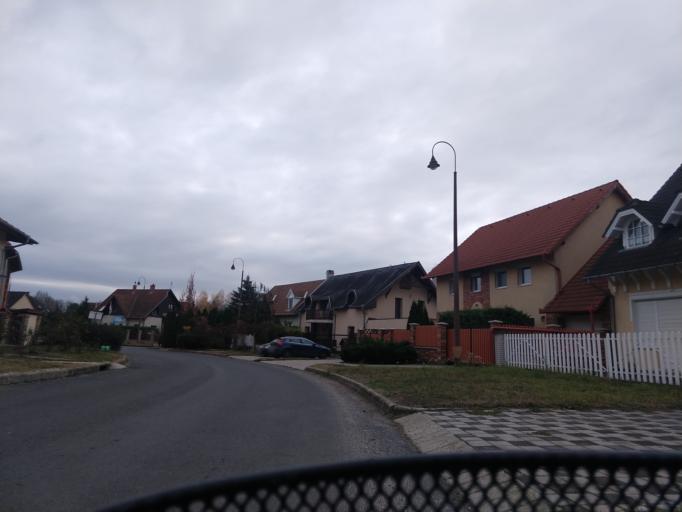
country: HU
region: Pest
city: Veresegyhaz
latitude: 47.6519
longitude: 19.2643
